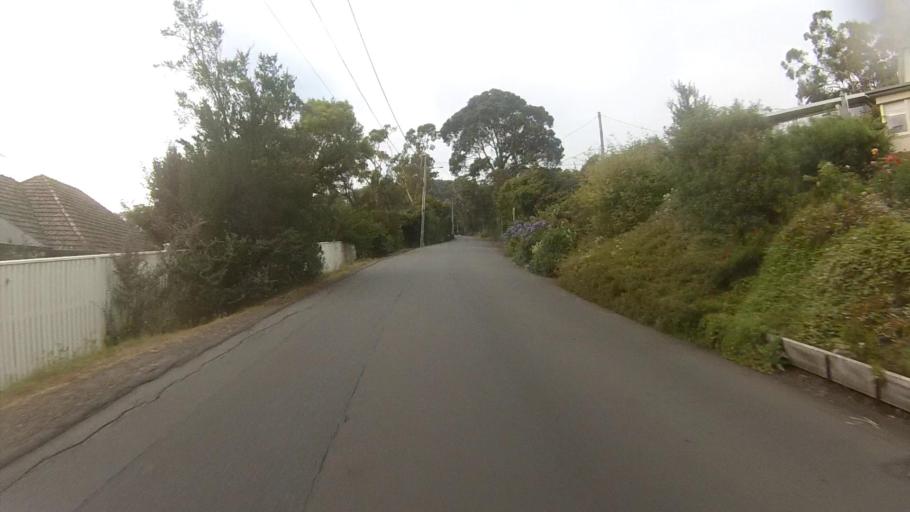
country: AU
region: Tasmania
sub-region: Hobart
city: Dynnyrne
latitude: -42.9084
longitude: 147.3284
